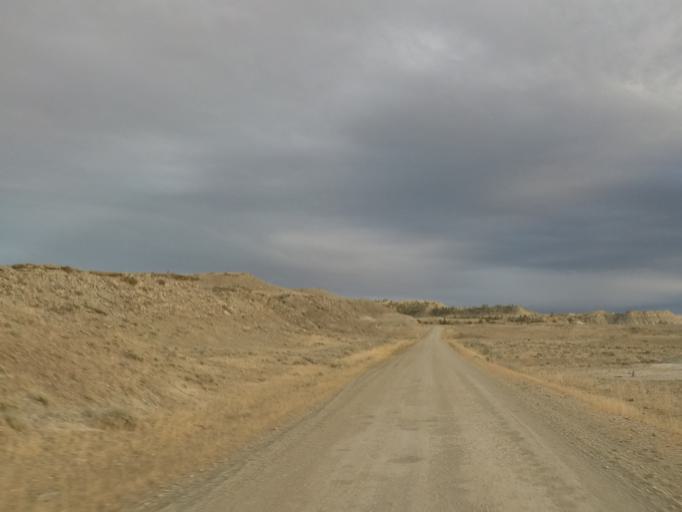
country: US
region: Montana
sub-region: Golden Valley County
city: Ryegate
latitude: 46.4516
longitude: -109.2609
